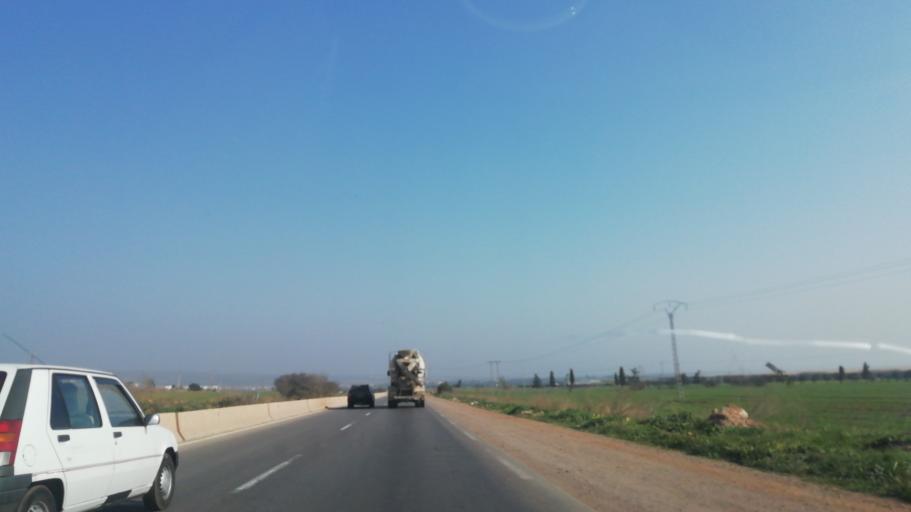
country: DZ
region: Oran
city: Bou Tlelis
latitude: 35.5576
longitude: -0.9359
